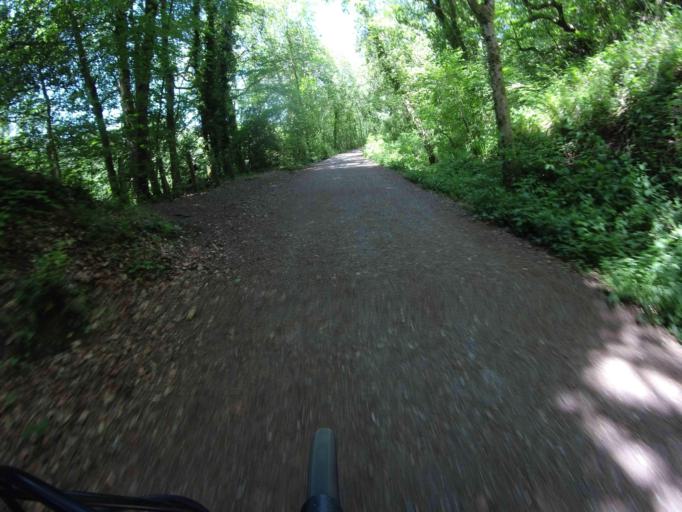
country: GB
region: England
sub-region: Devon
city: Bovey Tracey
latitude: 50.6016
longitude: -3.6964
